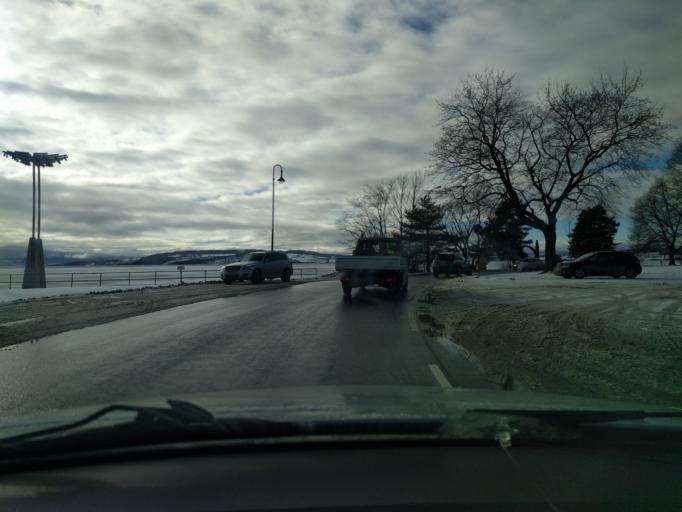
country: NO
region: Hedmark
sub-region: Hamar
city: Hamar
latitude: 60.7932
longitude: 11.0668
